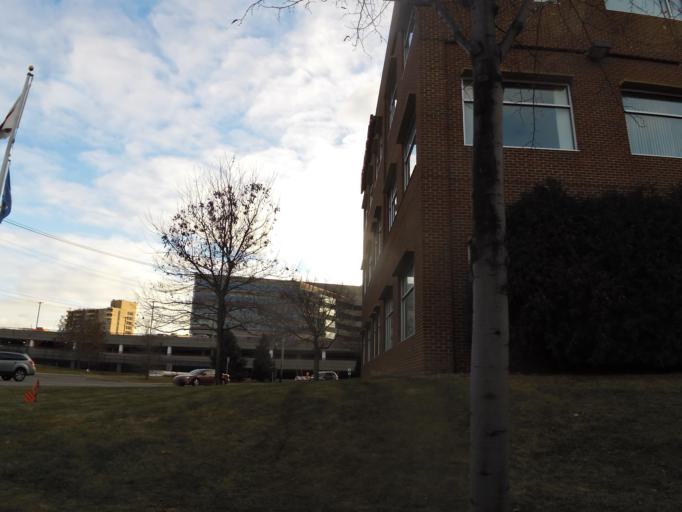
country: US
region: Minnesota
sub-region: Hennepin County
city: Minneapolis
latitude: 44.9775
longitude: -93.2481
